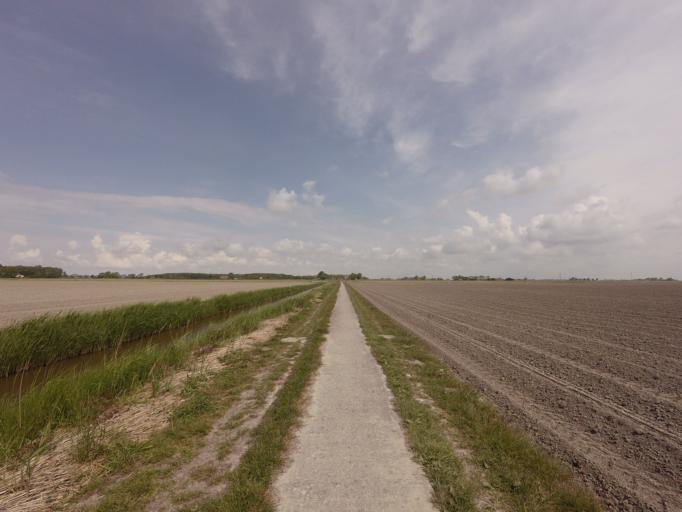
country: NL
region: Friesland
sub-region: Sudwest Fryslan
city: Bolsward
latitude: 53.1039
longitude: 5.4850
